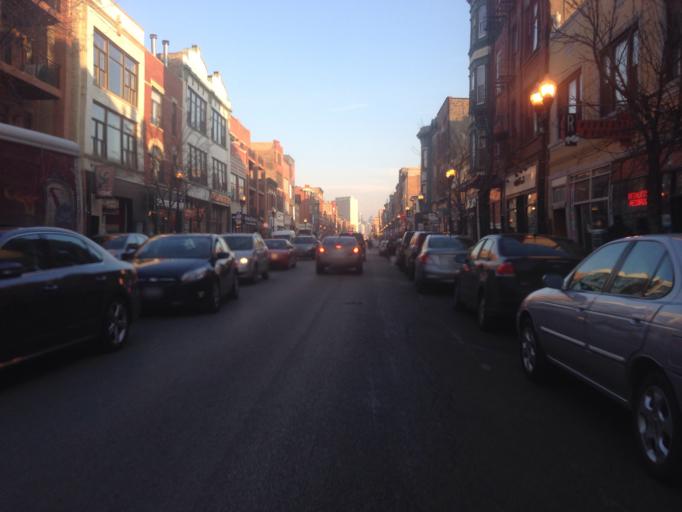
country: US
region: Illinois
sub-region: Cook County
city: Chicago
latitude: 41.9094
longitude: -87.6761
